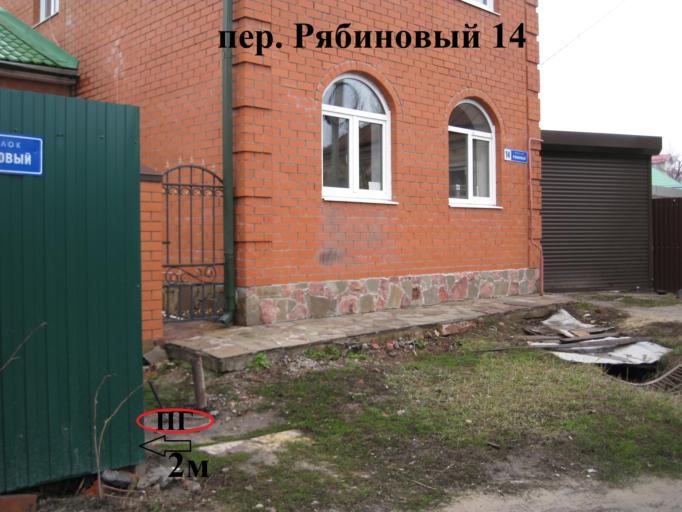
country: RU
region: Voronezj
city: Voronezh
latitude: 51.6343
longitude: 39.1738
